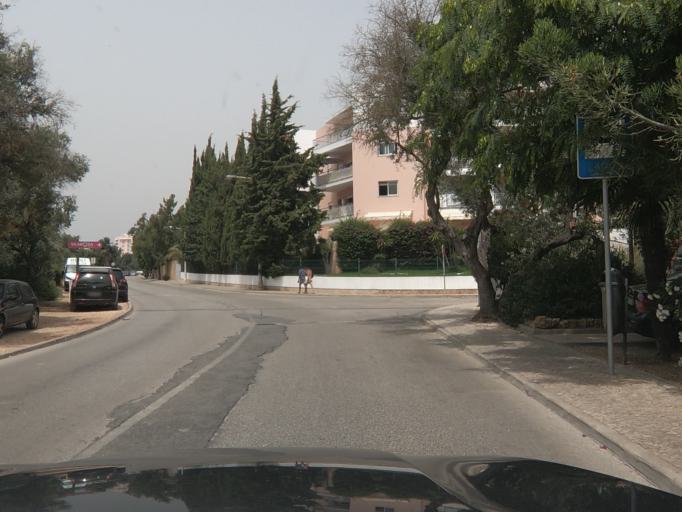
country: PT
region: Faro
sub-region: Portimao
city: Portimao
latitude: 37.1225
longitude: -8.5405
